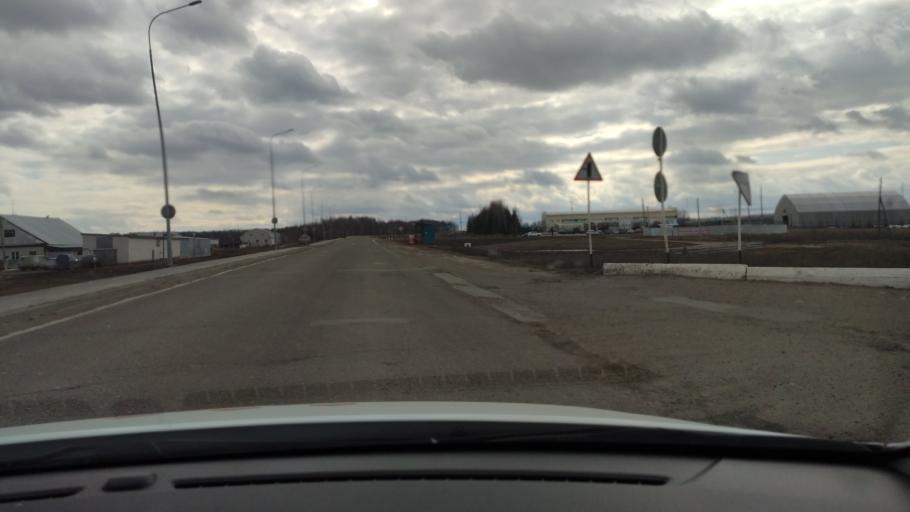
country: RU
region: Tatarstan
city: Vysokaya Gora
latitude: 56.1139
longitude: 49.1886
